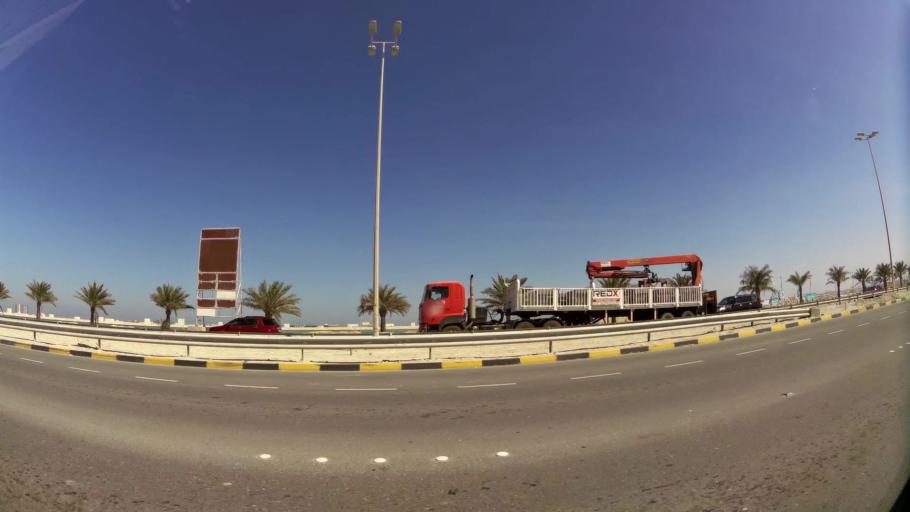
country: BH
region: Muharraq
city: Al Hadd
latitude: 26.2555
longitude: 50.6599
